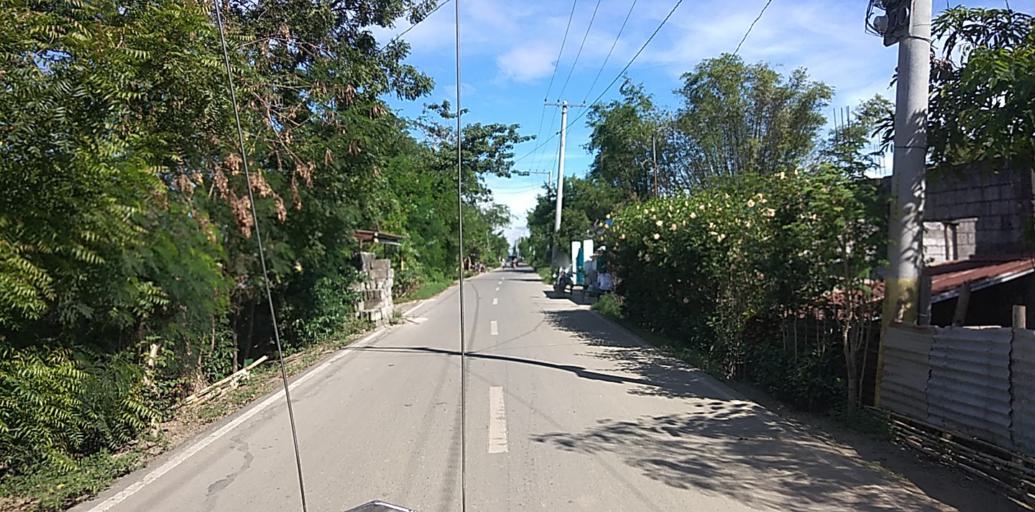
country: PH
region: Central Luzon
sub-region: Province of Pampanga
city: Candaba
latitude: 15.0788
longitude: 120.8083
